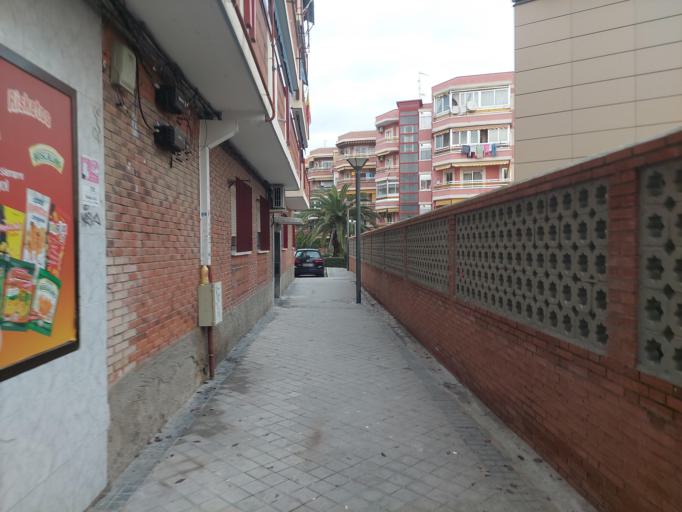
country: ES
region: Madrid
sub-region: Provincia de Madrid
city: Leganes
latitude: 40.3269
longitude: -3.7692
